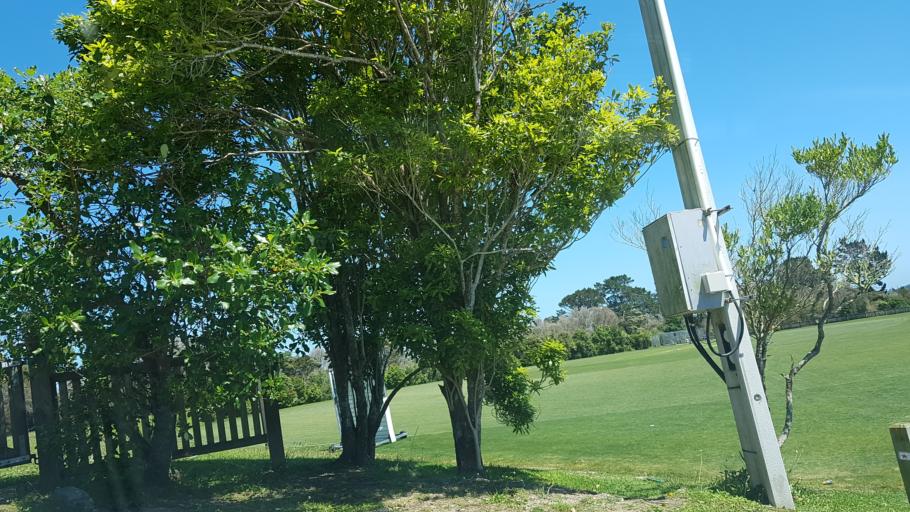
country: NZ
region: Auckland
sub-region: Auckland
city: North Shore
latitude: -36.8070
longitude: 174.7212
